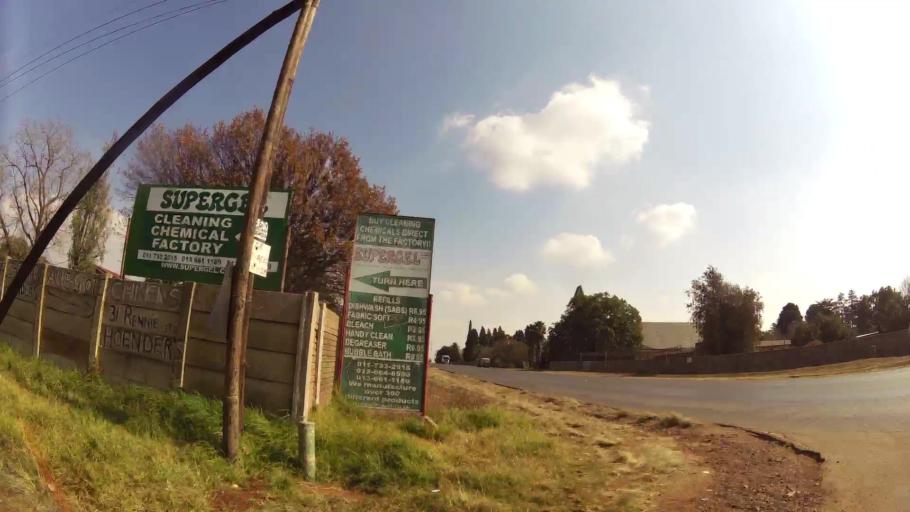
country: ZA
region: Gauteng
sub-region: Ekurhuleni Metropolitan Municipality
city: Springs
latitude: -26.1875
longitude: 28.5367
